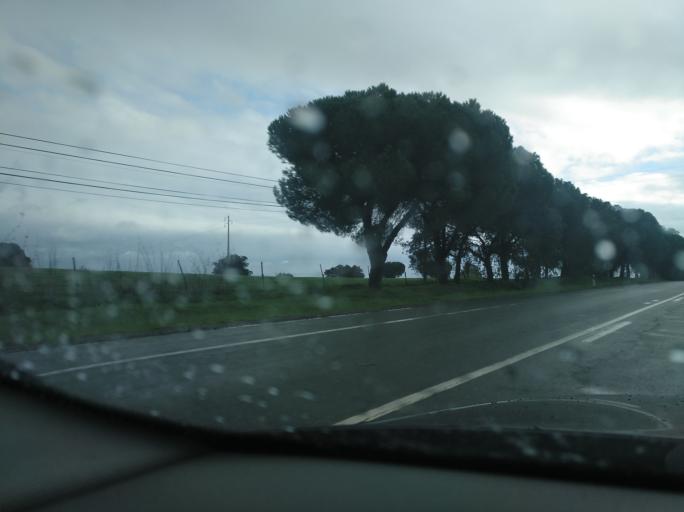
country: PT
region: Setubal
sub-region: Grandola
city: Grandola
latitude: 38.0997
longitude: -8.4184
